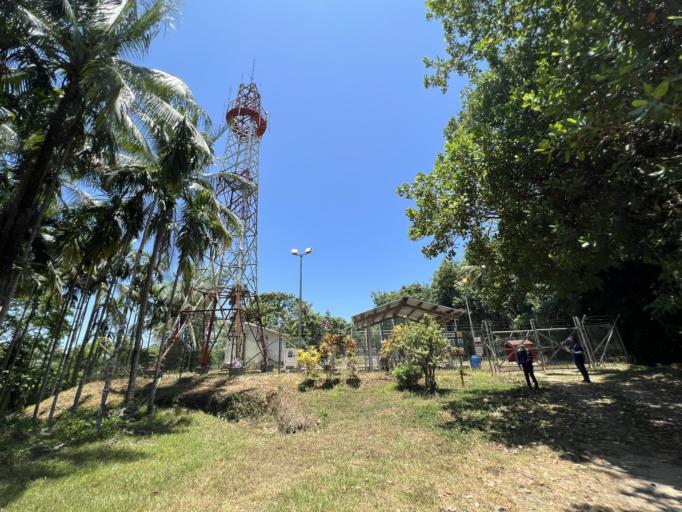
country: MM
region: Tanintharyi
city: Dawei
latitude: 14.5741
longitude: 97.9129
